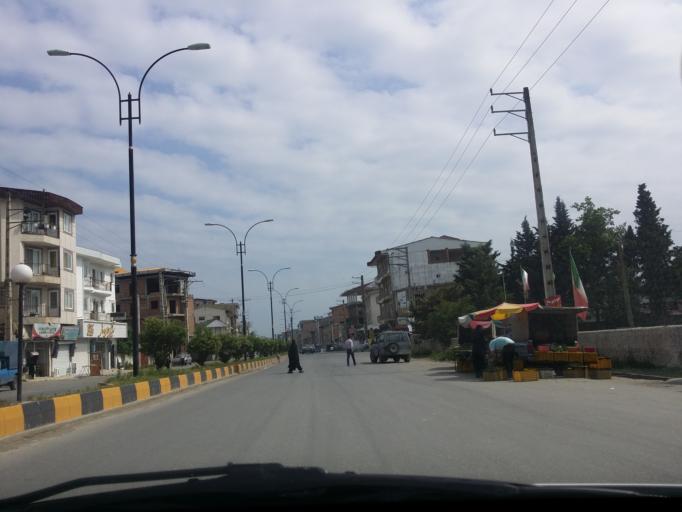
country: IR
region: Mazandaran
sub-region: Nowshahr
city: Nowshahr
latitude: 36.6306
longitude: 51.4856
